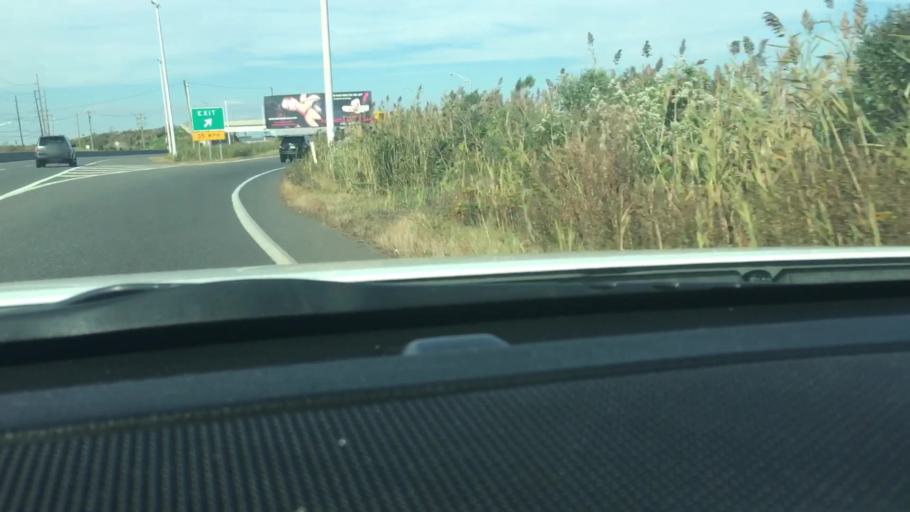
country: US
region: New Jersey
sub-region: Atlantic County
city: Pleasantville
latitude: 39.3940
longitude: -74.4909
